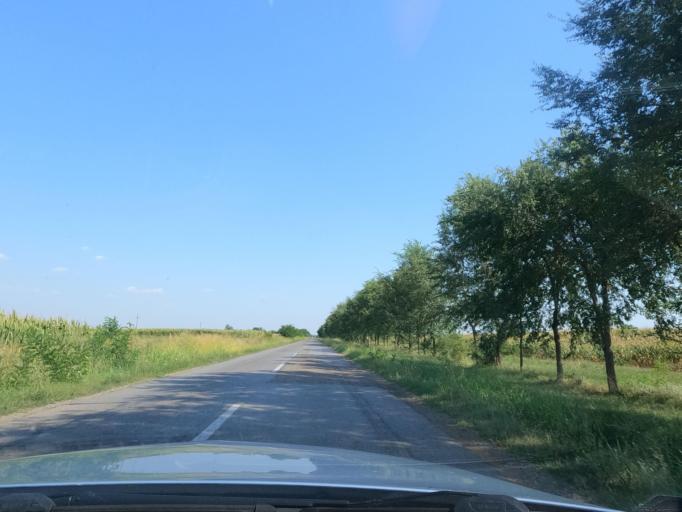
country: RS
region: Autonomna Pokrajina Vojvodina
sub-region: Juznobacki Okrug
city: Becej
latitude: 45.6495
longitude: 19.9781
